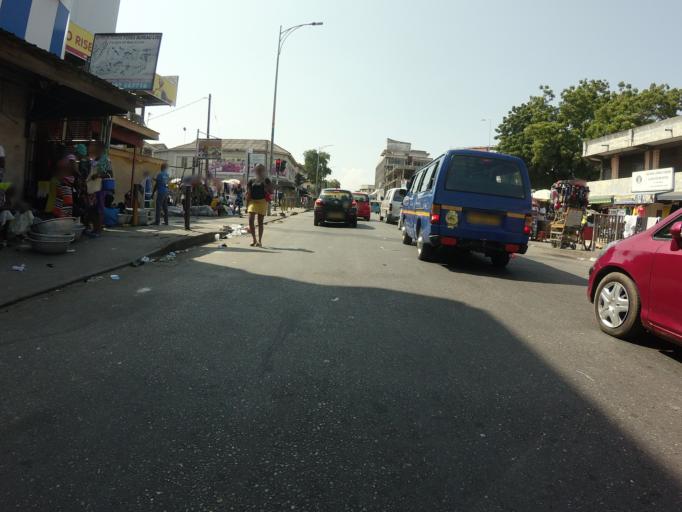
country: GH
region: Greater Accra
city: Accra
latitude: 5.5499
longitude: -0.2076
